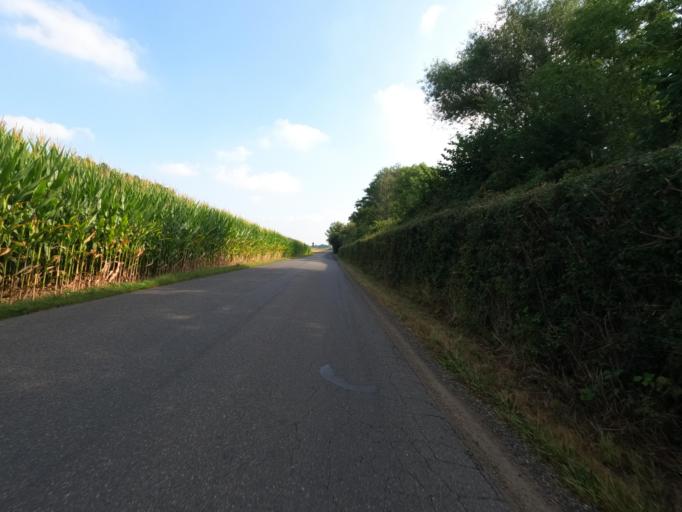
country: DE
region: North Rhine-Westphalia
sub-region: Regierungsbezirk Koln
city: Heinsberg
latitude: 51.0827
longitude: 6.0837
